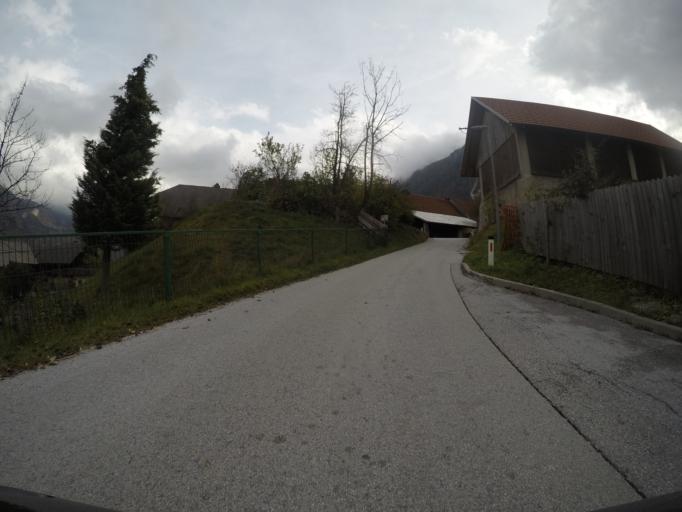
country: SI
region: Jesenice
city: Hrusica
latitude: 46.4613
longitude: 13.9429
